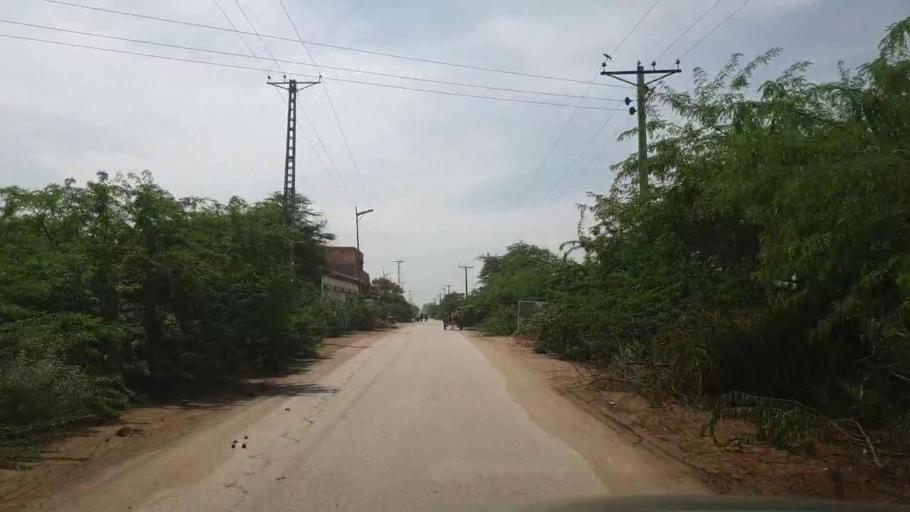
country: PK
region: Sindh
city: Kot Diji
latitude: 27.1617
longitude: 68.9562
